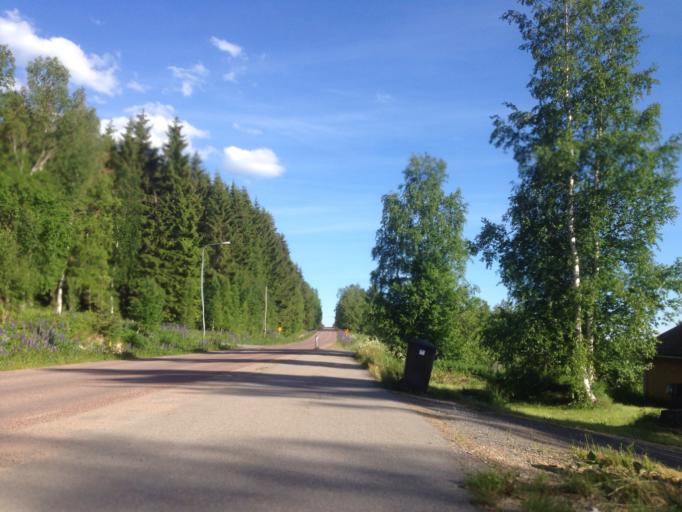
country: SE
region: Dalarna
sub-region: Ludvika Kommun
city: Ludvika
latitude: 60.1183
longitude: 15.2037
